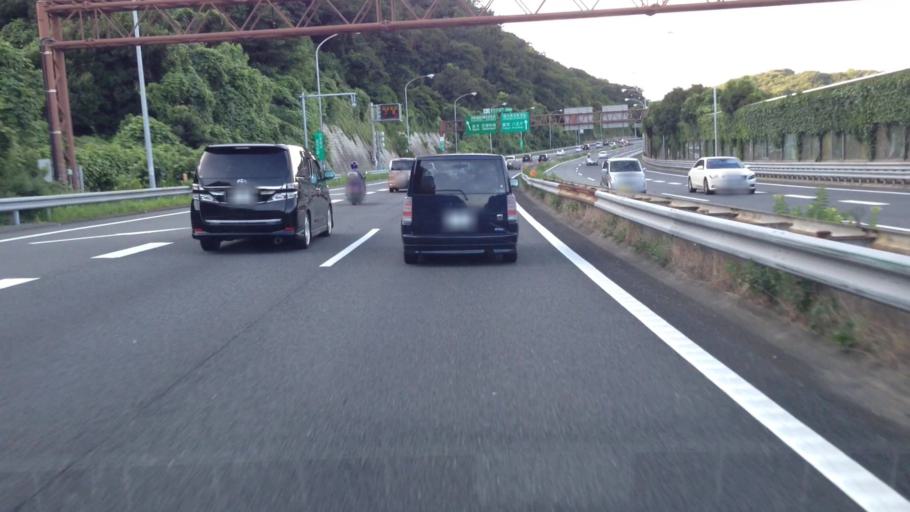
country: JP
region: Kanagawa
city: Zushi
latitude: 35.3404
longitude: 139.5907
